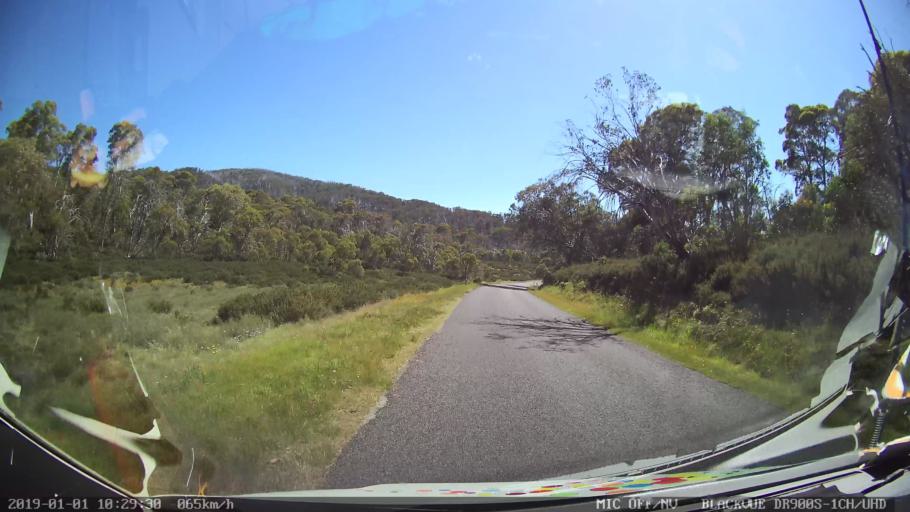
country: AU
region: New South Wales
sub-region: Snowy River
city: Jindabyne
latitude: -36.0538
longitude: 148.2480
